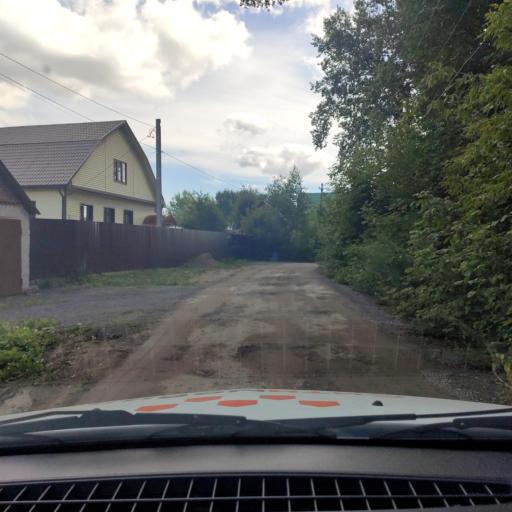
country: RU
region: Bashkortostan
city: Ufa
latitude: 54.7102
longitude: 55.9363
